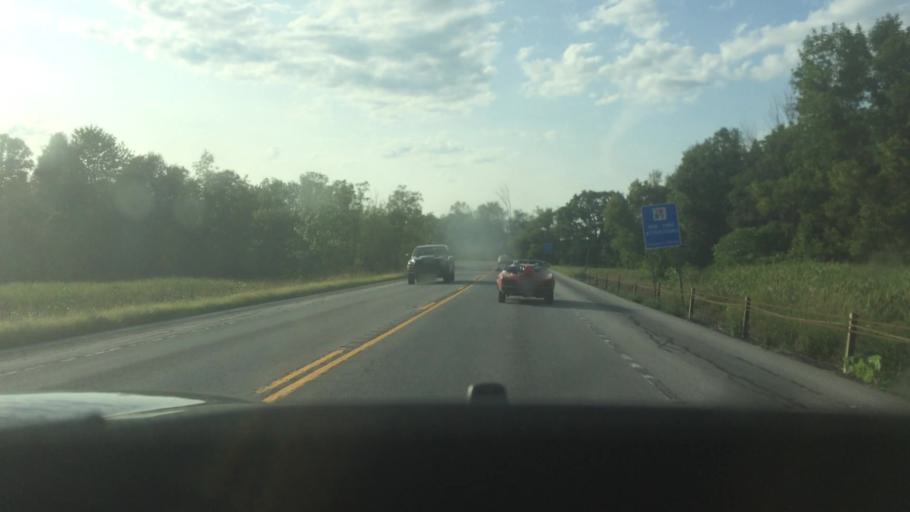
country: US
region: New York
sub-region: St. Lawrence County
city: Canton
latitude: 44.6176
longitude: -75.2219
